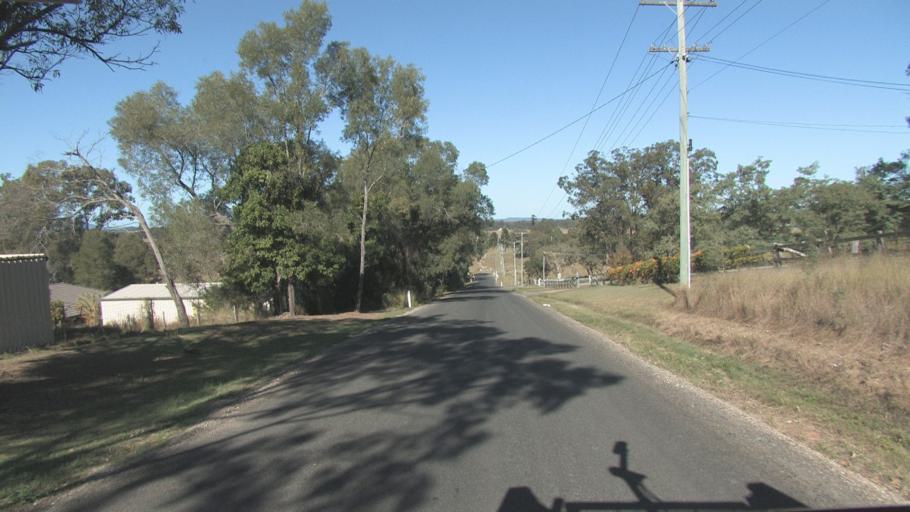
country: AU
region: Queensland
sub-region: Logan
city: Chambers Flat
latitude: -27.7572
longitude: 153.0693
